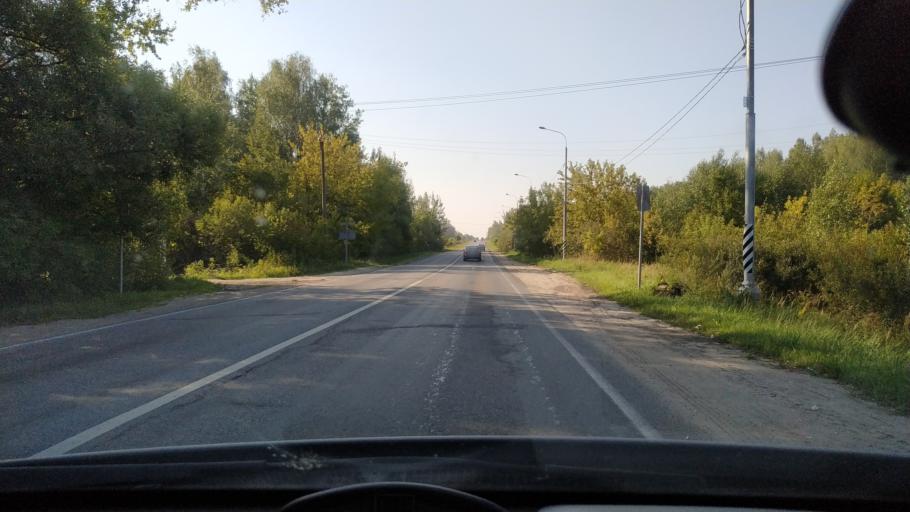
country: RU
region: Moskovskaya
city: Tugolesskiy Bor
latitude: 55.5594
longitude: 39.7023
